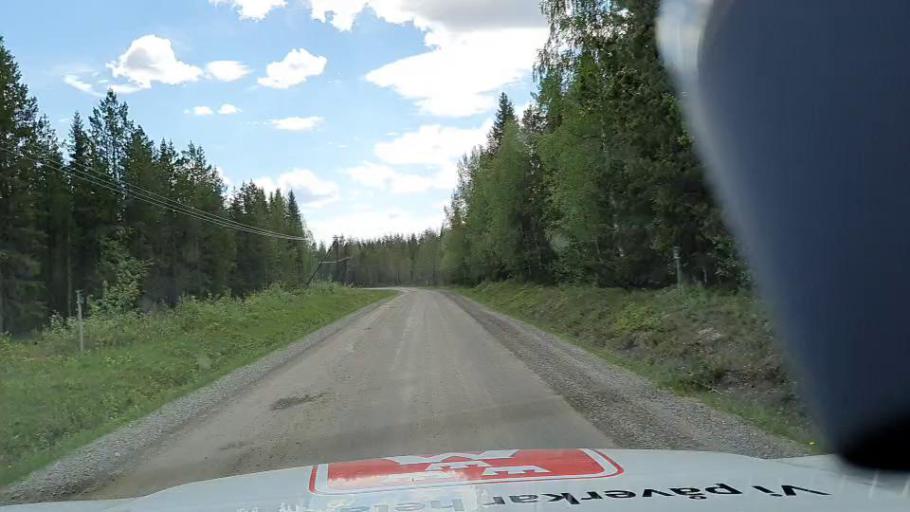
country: SE
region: Jaemtland
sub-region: Stroemsunds Kommun
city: Stroemsund
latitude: 64.5325
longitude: 15.5943
